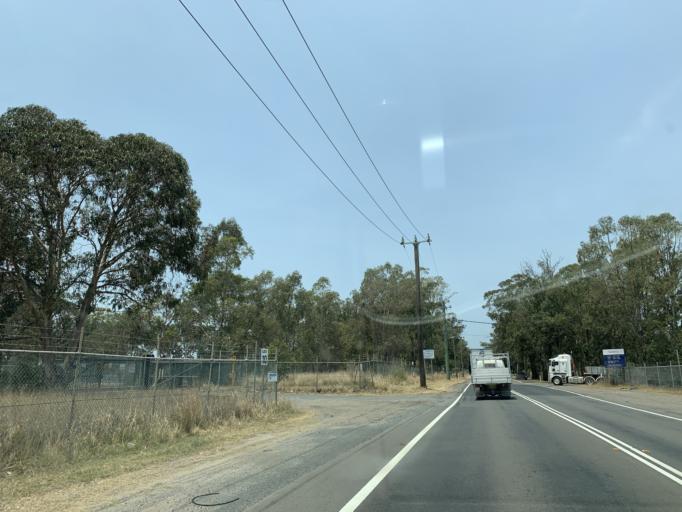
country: AU
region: New South Wales
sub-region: Fairfield
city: Horsley Park
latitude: -33.8236
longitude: 150.8709
